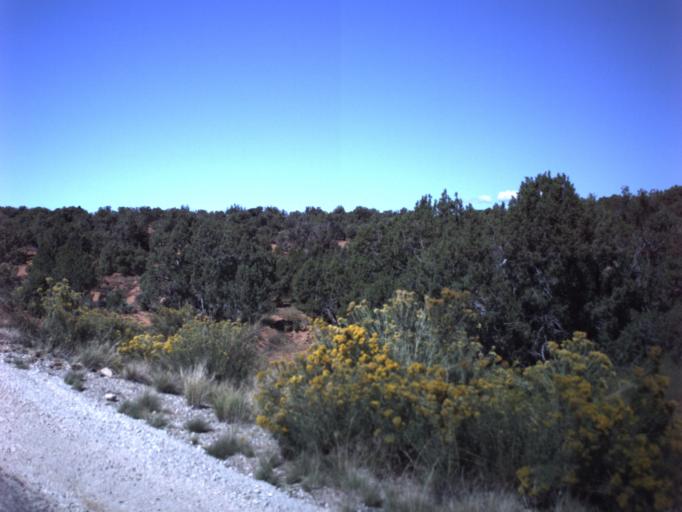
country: US
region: Utah
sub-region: San Juan County
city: Blanding
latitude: 37.5778
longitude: -109.5164
